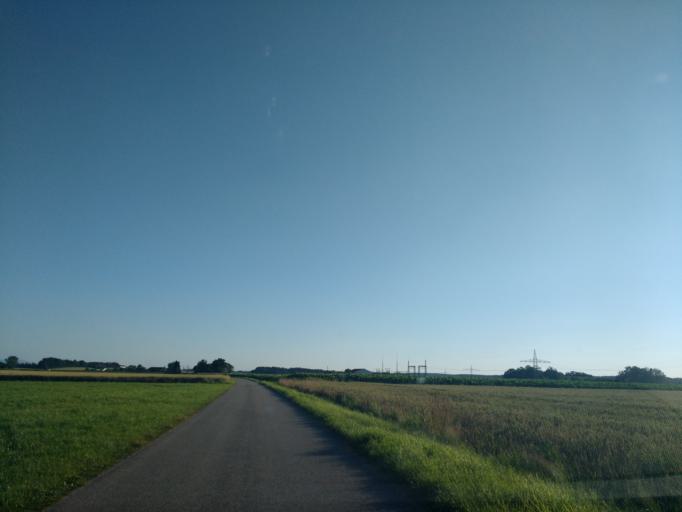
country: DE
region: Bavaria
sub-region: Upper Bavaria
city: Taufkirchen
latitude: 48.1464
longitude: 12.4736
